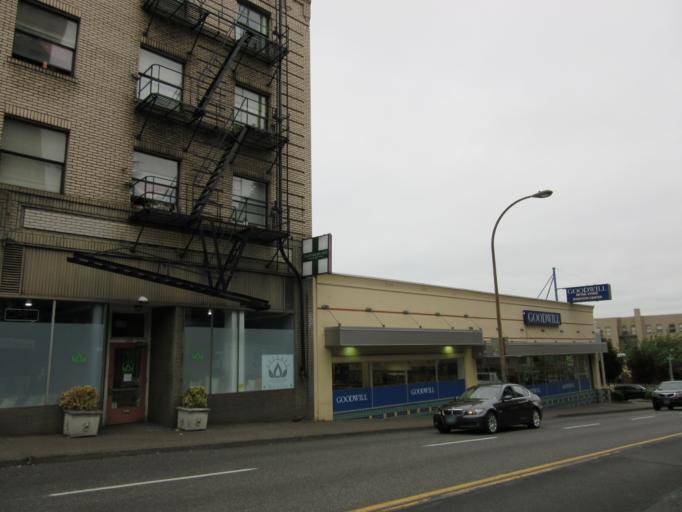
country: US
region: Oregon
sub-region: Multnomah County
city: Portland
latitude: 45.5233
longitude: -122.6971
